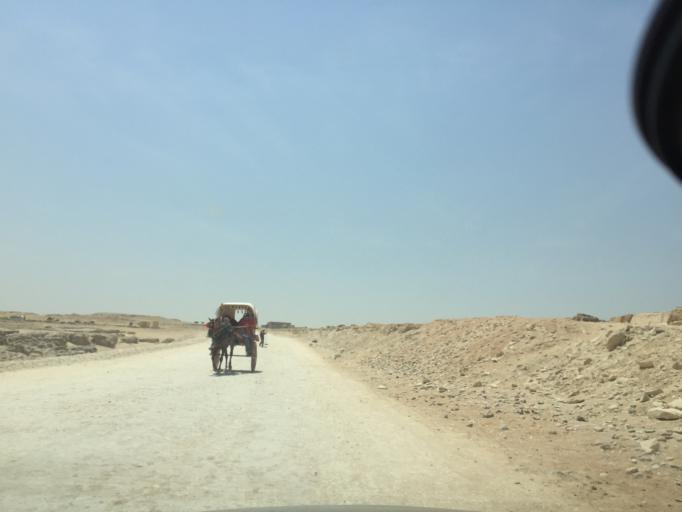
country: EG
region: Al Jizah
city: Al Jizah
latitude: 29.9779
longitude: 31.1311
